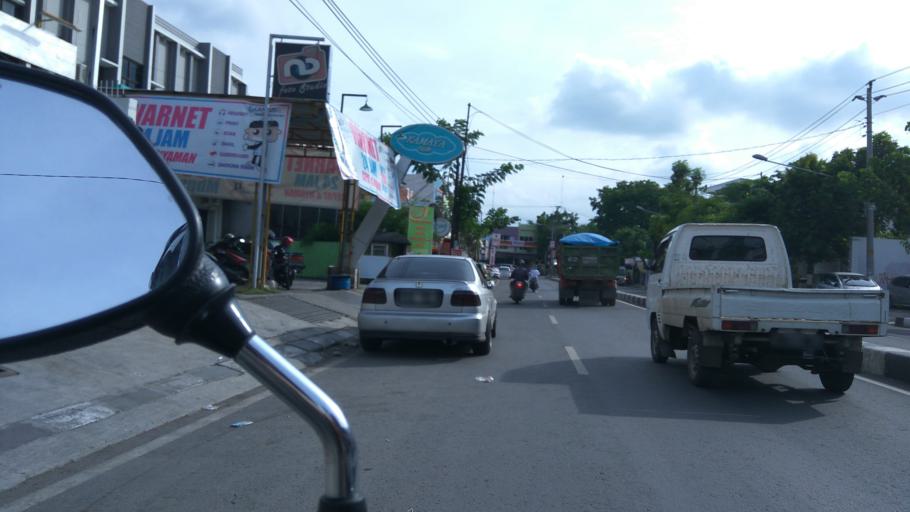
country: ID
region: Central Java
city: Semarang
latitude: -7.0243
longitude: 110.4617
